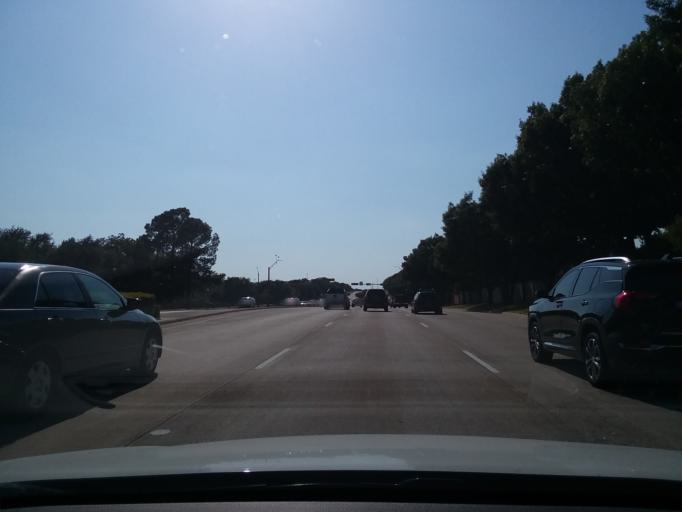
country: US
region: Texas
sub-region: Denton County
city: Flower Mound
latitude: 33.0139
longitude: -97.0600
